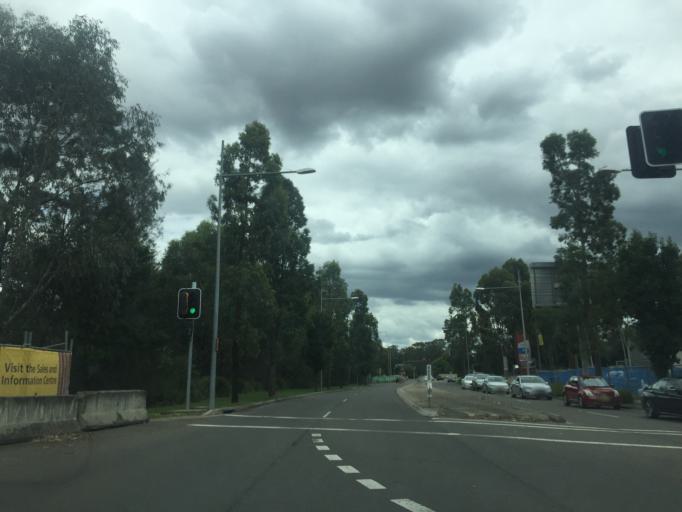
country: AU
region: New South Wales
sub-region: Blacktown
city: Rouse Hill
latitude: -33.6922
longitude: 150.9269
